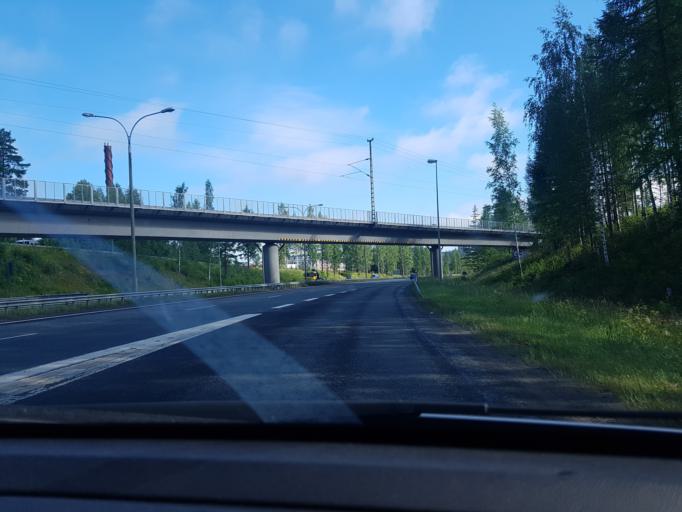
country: FI
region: Northern Savo
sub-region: Kuopio
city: Kuopio
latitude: 62.8875
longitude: 27.6372
